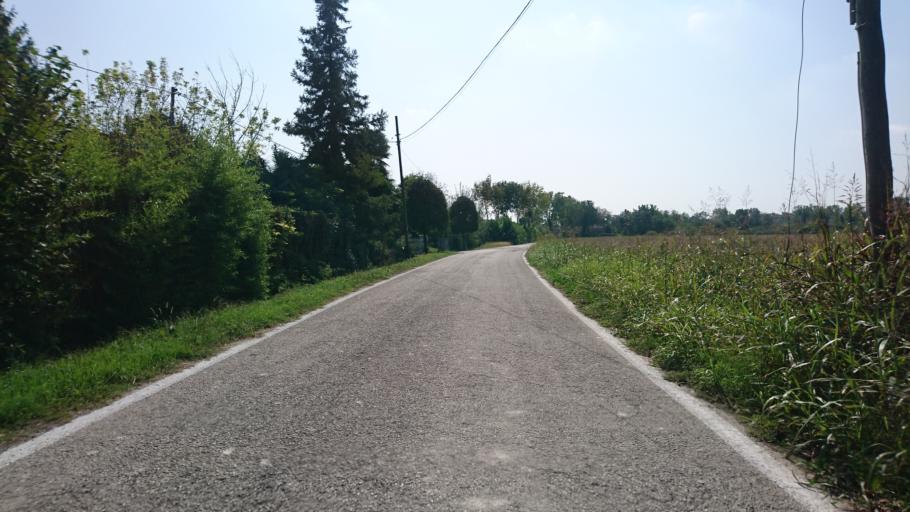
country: IT
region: Veneto
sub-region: Provincia di Padova
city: Piazzola sul Brenta
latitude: 45.5740
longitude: 11.7718
